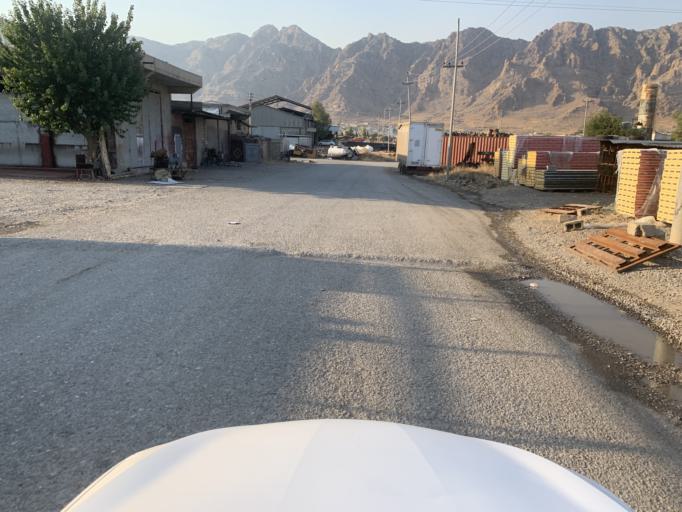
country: IQ
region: As Sulaymaniyah
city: Raniye
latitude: 36.2464
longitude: 44.8891
